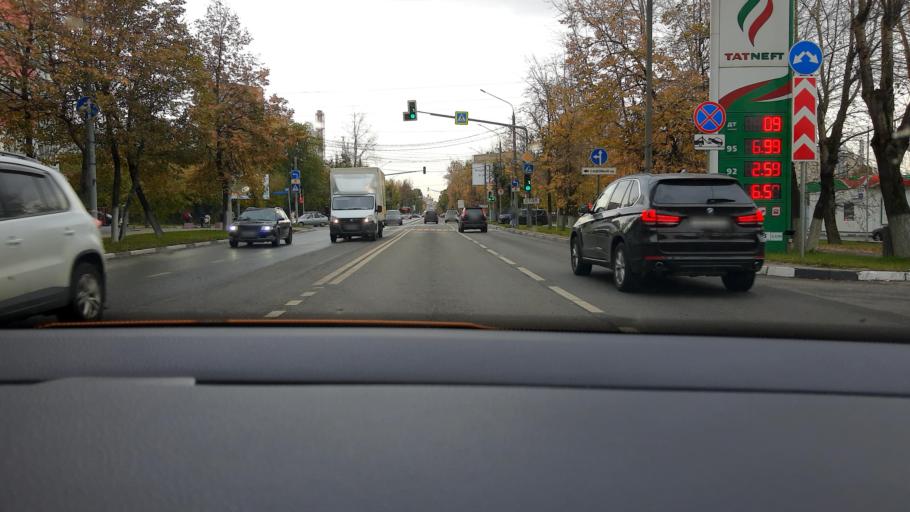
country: RU
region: Moskovskaya
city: Reutov
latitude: 55.7668
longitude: 37.8487
